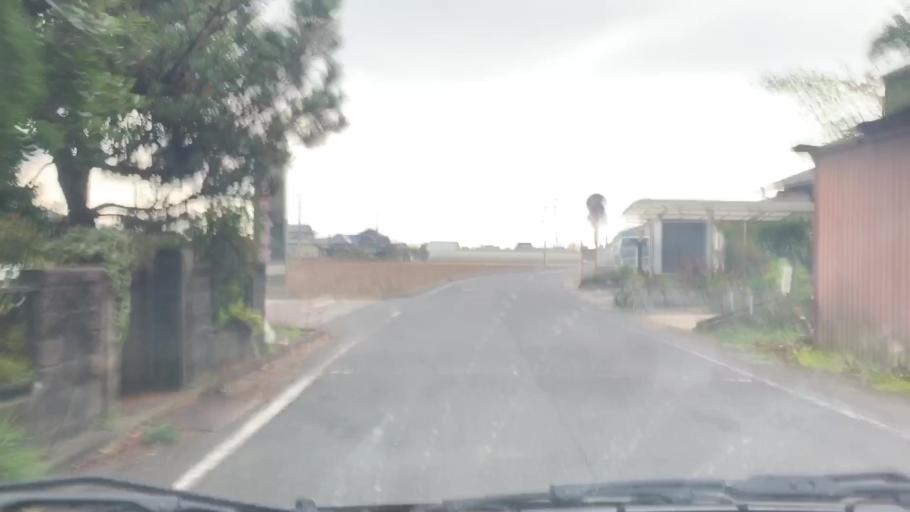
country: JP
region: Saga Prefecture
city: Kashima
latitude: 33.1230
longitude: 130.0563
